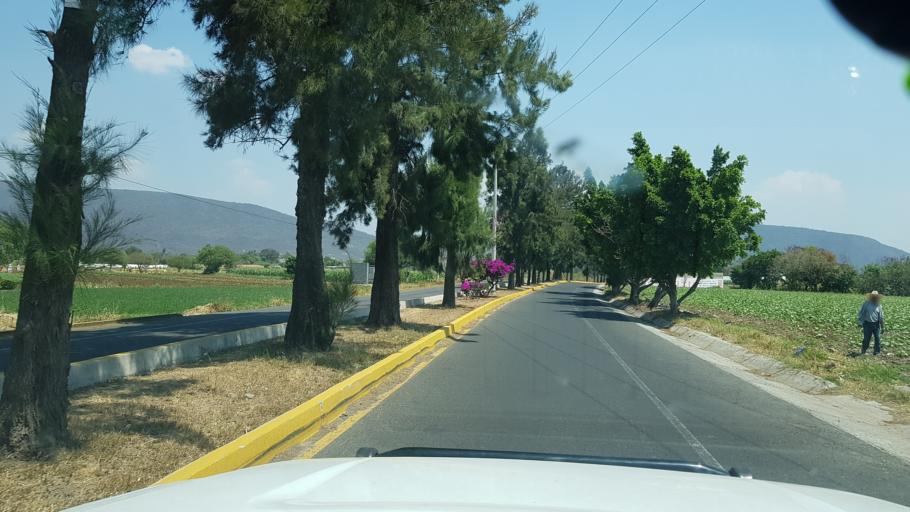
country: MX
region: Puebla
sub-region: Huaquechula
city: Cacaloxuchitl
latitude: 18.7918
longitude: -98.4631
